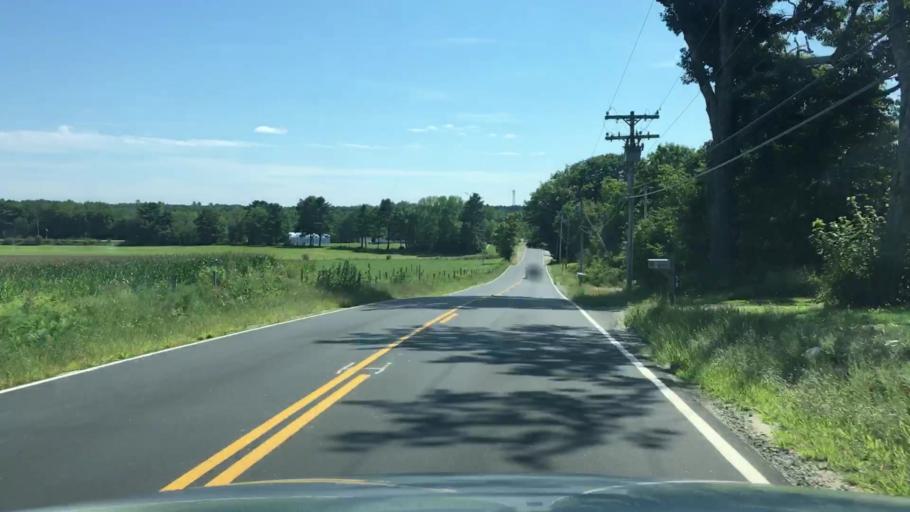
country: US
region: Maine
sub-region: Sagadahoc County
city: Topsham
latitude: 43.9572
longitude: -69.9747
